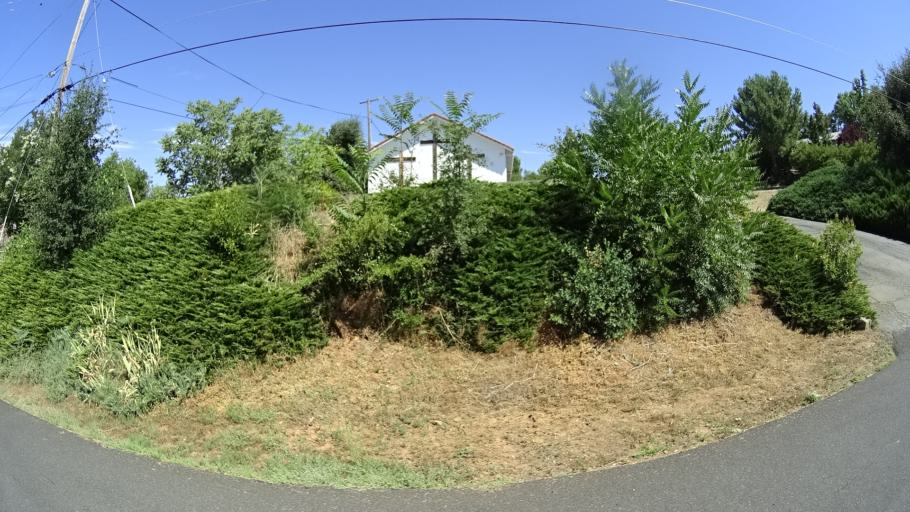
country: US
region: California
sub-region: Calaveras County
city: Angels Camp
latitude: 38.0716
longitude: -120.5370
